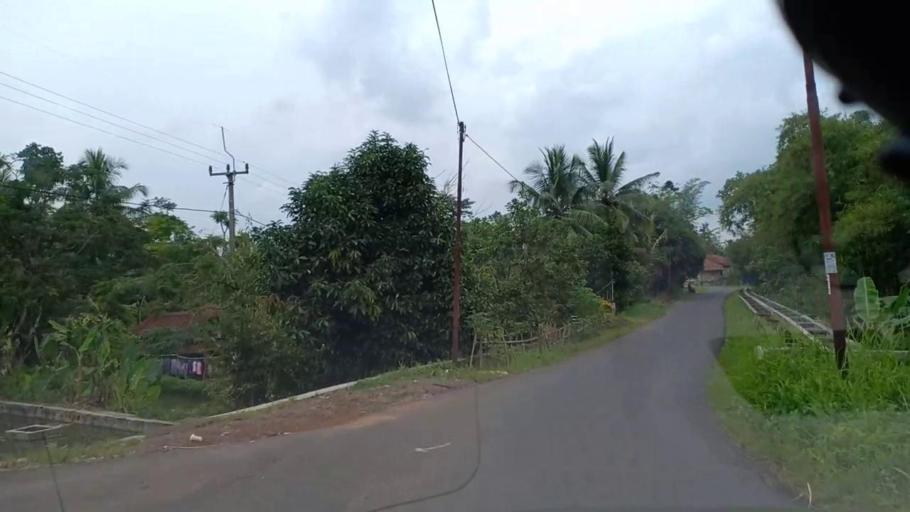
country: ID
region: West Java
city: Kertasari
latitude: -7.3376
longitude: 108.2790
